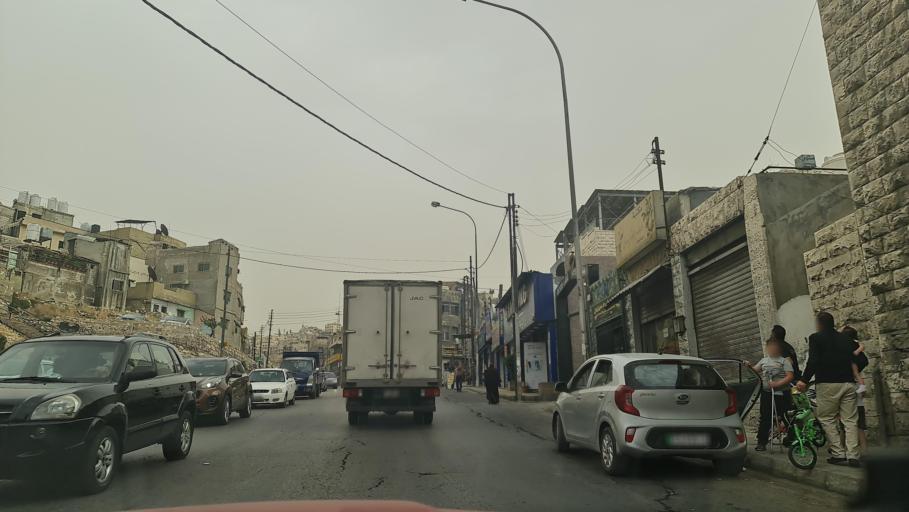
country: JO
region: Amman
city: Amman
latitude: 31.9437
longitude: 35.9291
